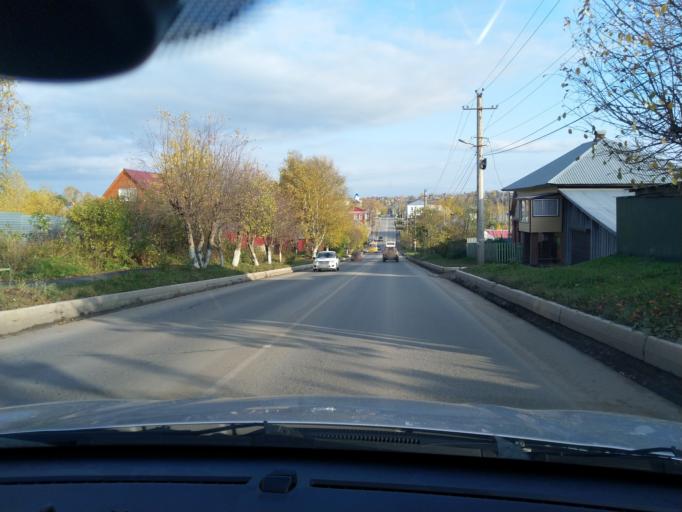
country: RU
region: Perm
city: Dobryanka
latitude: 58.4617
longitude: 56.4062
